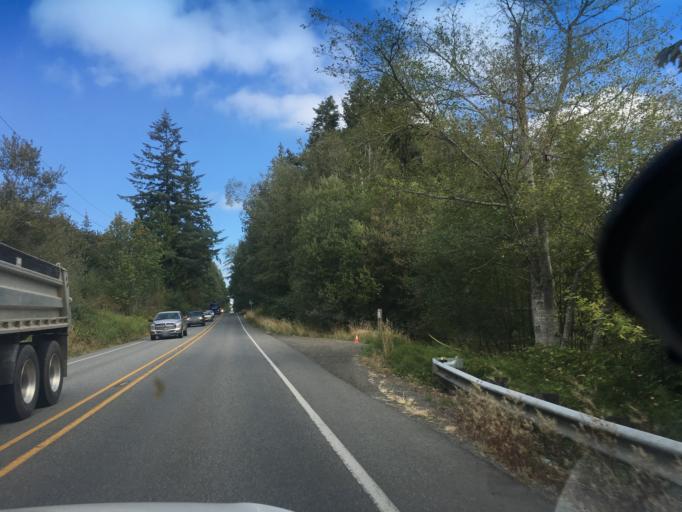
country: US
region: Washington
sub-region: Kitsap County
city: Lofall
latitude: 47.8421
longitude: -122.5871
